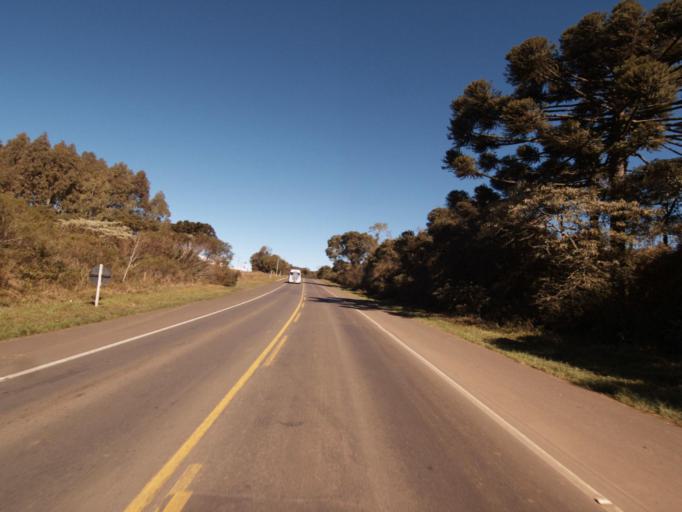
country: BR
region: Santa Catarina
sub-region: Xanxere
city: Xanxere
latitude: -26.8779
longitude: -52.1603
